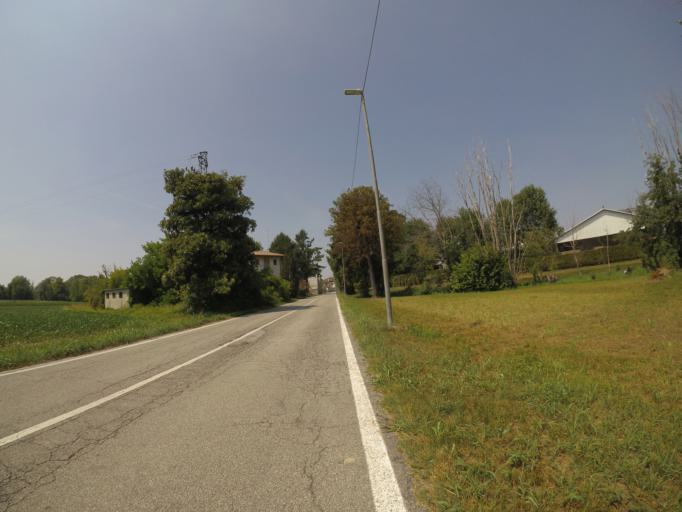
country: IT
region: Friuli Venezia Giulia
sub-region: Provincia di Udine
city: Varmo
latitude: 45.8974
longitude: 12.9663
